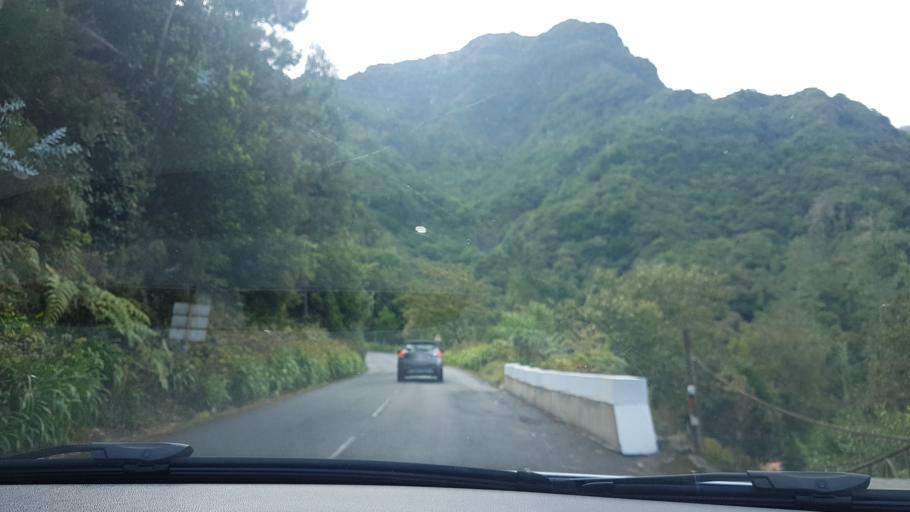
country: PT
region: Madeira
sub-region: Sao Vicente
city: Sao Vicente
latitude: 32.7659
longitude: -17.0290
